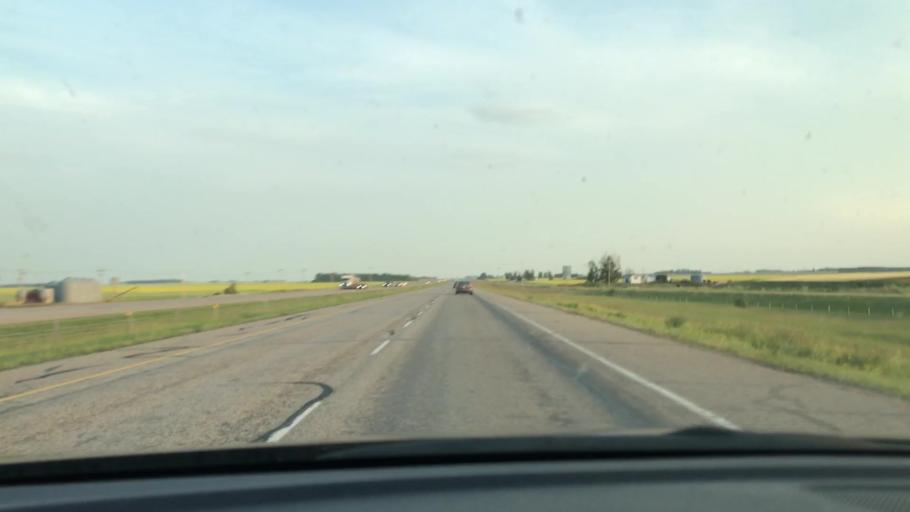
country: CA
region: Alberta
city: Olds
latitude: 51.8511
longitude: -114.0256
